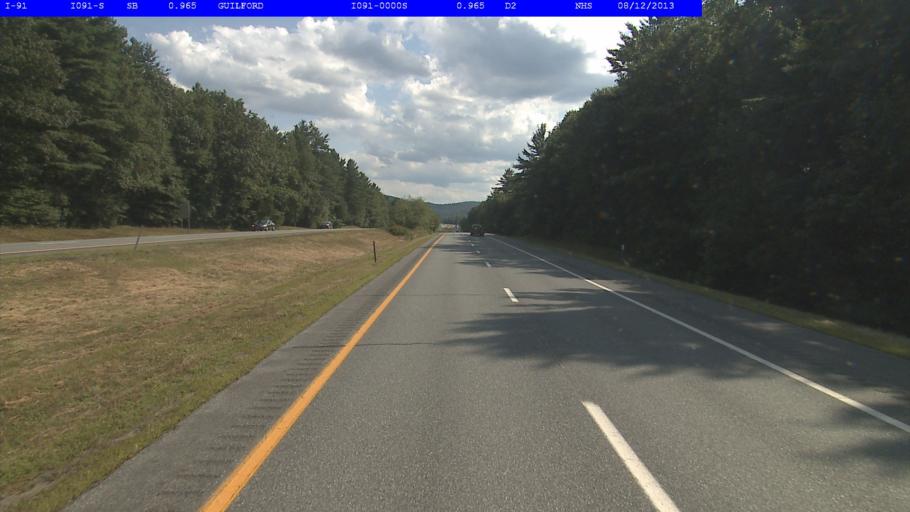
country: US
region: Massachusetts
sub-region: Franklin County
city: Bernardston
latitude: 42.7439
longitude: -72.5669
